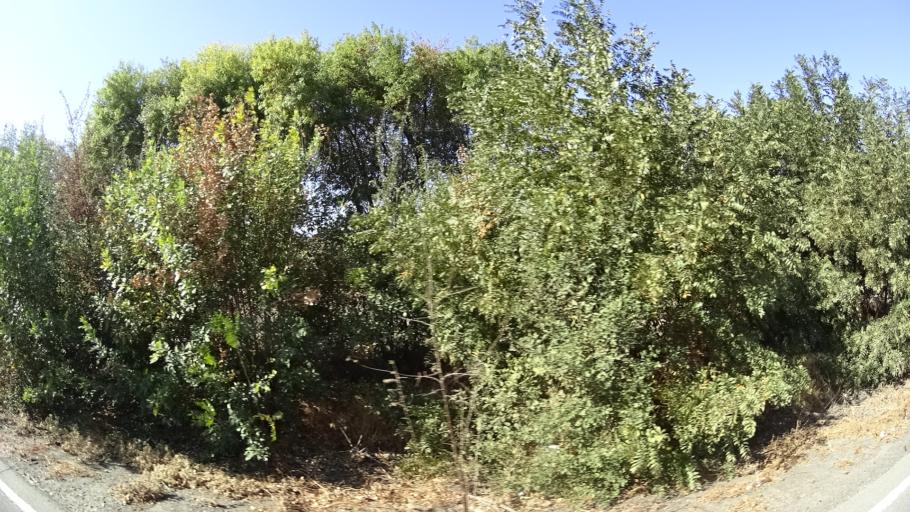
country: US
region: California
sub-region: Yolo County
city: Woodland
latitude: 38.6458
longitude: -121.7661
